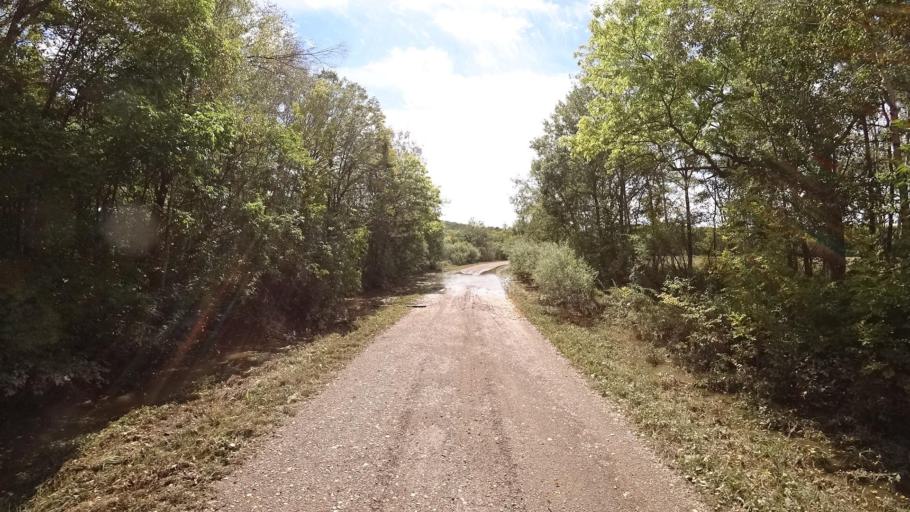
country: RU
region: Primorskiy
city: Yakovlevka
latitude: 44.6634
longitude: 133.7505
